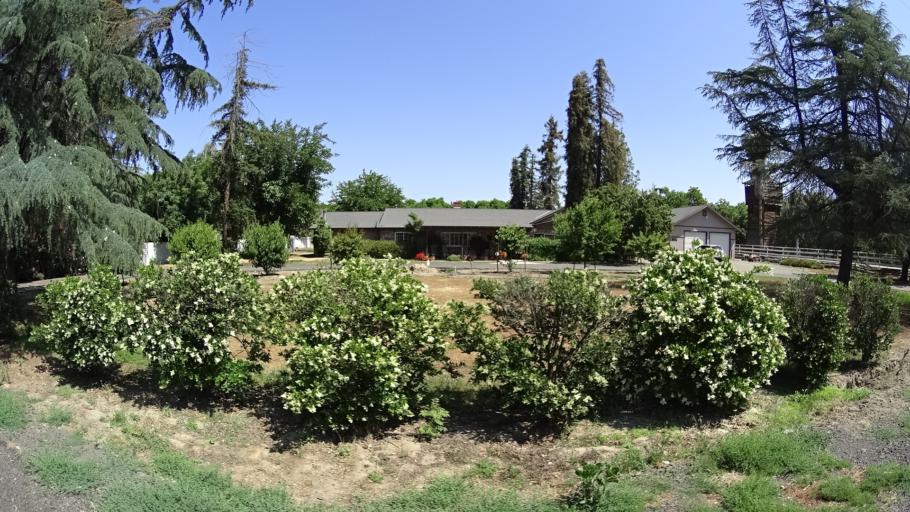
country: US
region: California
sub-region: Kings County
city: Lucerne
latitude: 36.3719
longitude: -119.6487
